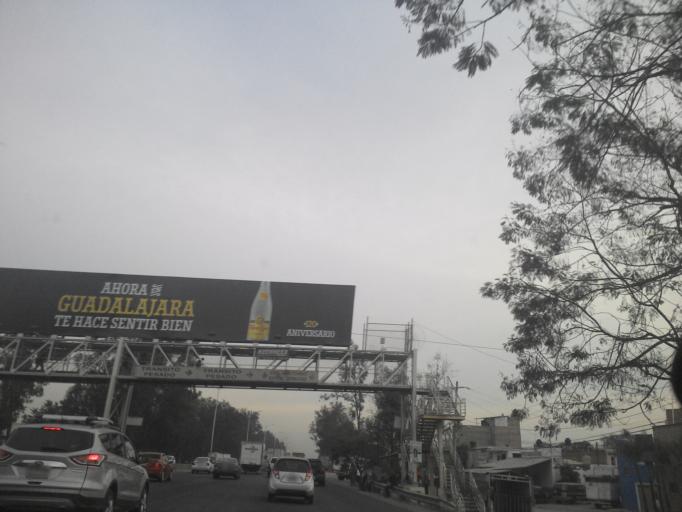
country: MX
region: Jalisco
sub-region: San Pedro Tlaquepaque
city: Paseo del Prado
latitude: 20.5983
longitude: -103.3924
